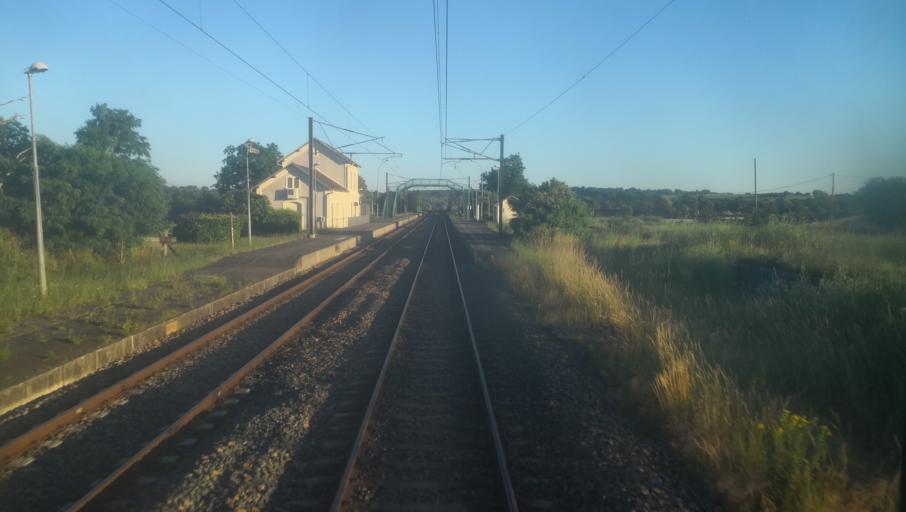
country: FR
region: Bourgogne
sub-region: Departement de la Nievre
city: Saint-Pierre-le-Moutier
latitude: 46.7940
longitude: 3.1117
